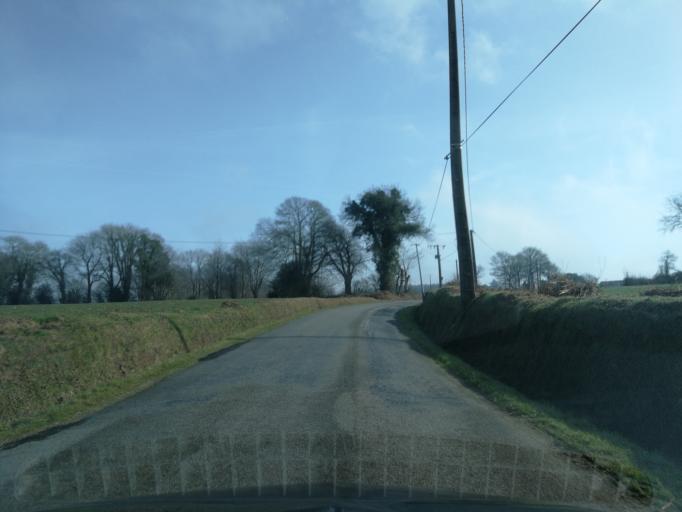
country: FR
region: Brittany
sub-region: Departement du Morbihan
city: La Vraie-Croix
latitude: 47.7097
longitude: -2.5071
